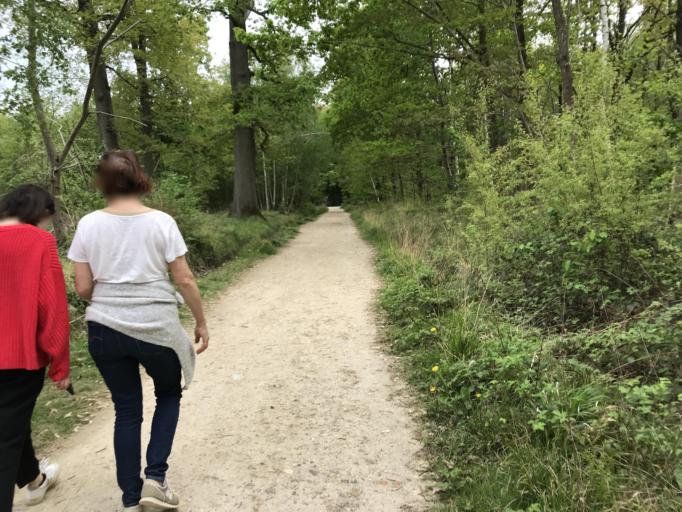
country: FR
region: Ile-de-France
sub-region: Departement de l'Essonne
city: Igny
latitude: 48.7528
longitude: 2.2402
